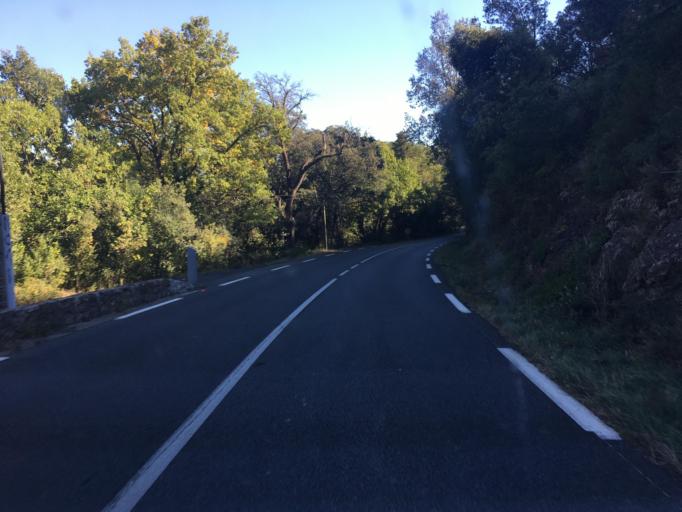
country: FR
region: Languedoc-Roussillon
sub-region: Departement de l'Herault
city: Nebian
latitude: 43.6107
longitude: 3.3947
